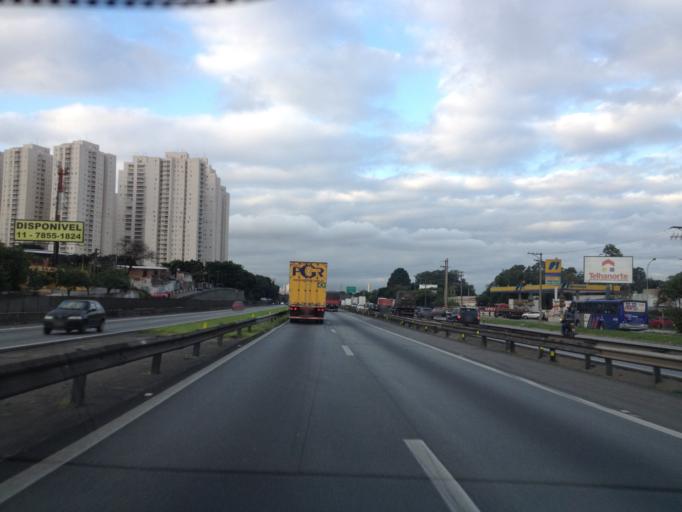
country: BR
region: Sao Paulo
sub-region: Guarulhos
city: Guarulhos
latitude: -23.4875
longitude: -46.5435
